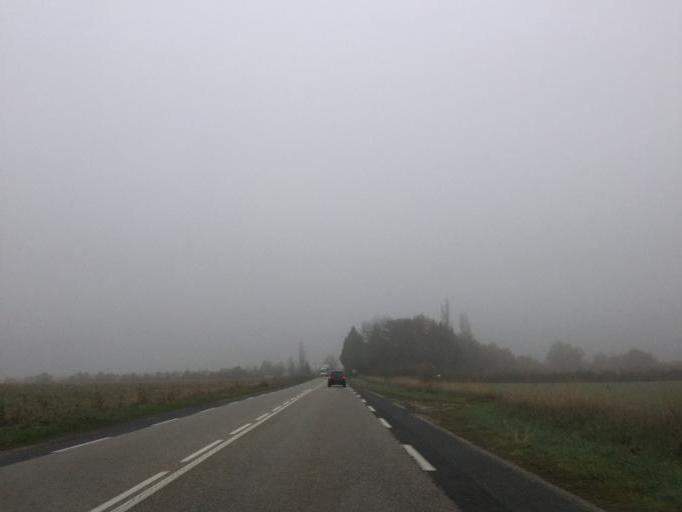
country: FR
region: Rhone-Alpes
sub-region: Departement de l'Ain
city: Mionnay
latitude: 45.9061
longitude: 4.9360
